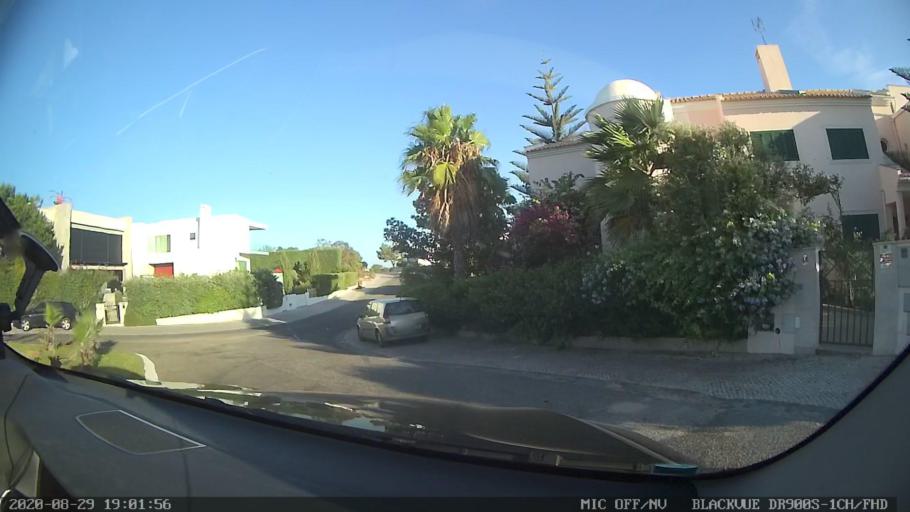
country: PT
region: Setubal
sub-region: Setubal
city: Setubal
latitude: 38.4554
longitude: -8.8629
